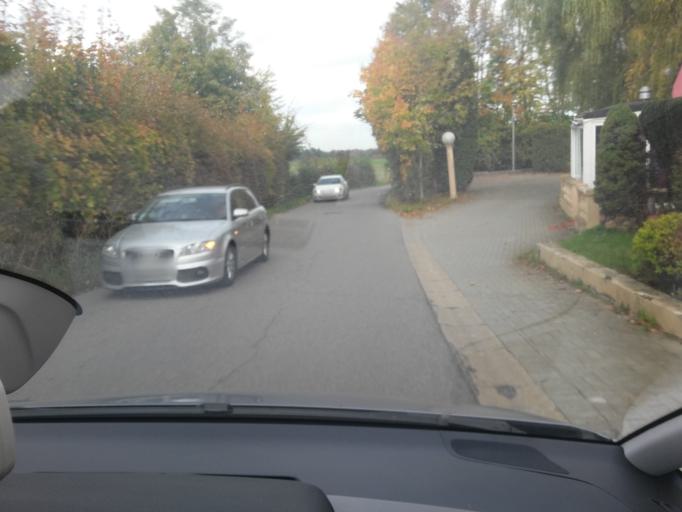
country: BE
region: Wallonia
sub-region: Province du Luxembourg
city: Arlon
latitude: 49.7070
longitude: 5.8045
